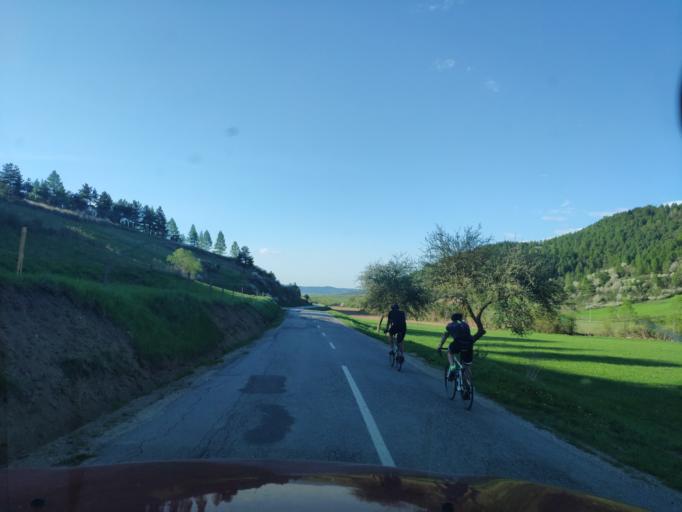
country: SK
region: Presovsky
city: Spisske Podhradie
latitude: 49.0838
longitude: 20.8467
